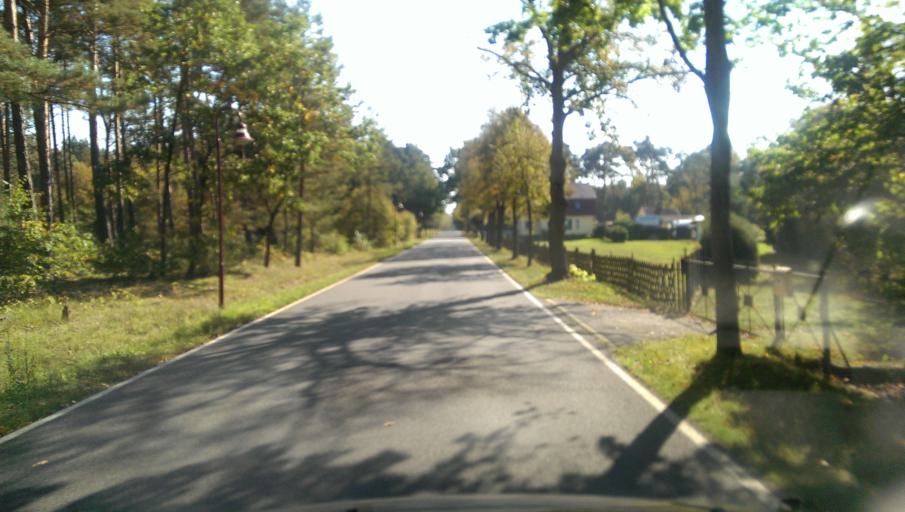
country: DE
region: Brandenburg
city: Halbe
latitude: 52.0515
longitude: 13.7138
